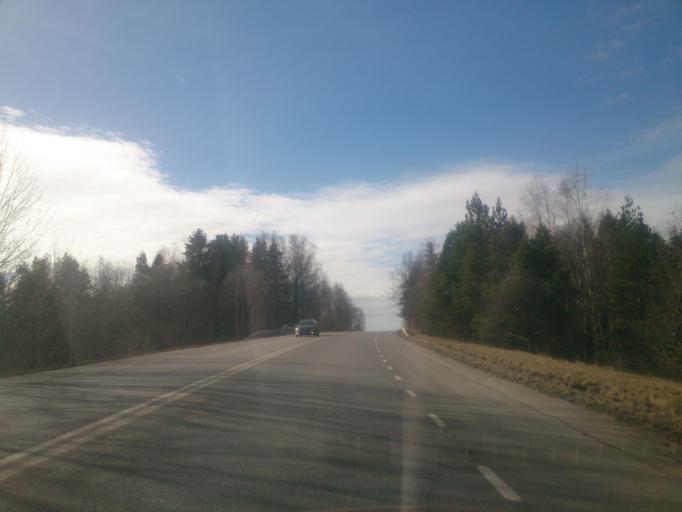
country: SE
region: OEstergoetland
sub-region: Norrkopings Kommun
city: Kimstad
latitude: 58.5036
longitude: 15.9788
